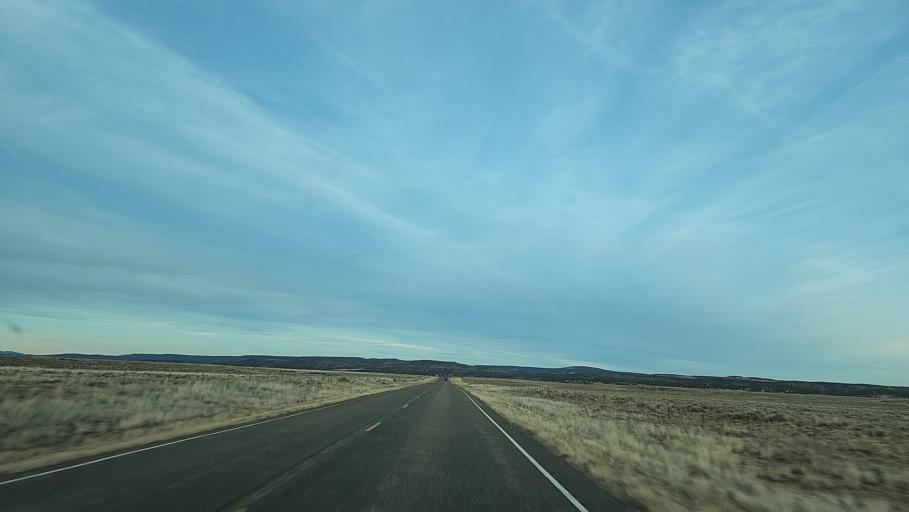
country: US
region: New Mexico
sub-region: Cibola County
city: Grants
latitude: 34.7012
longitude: -108.0335
